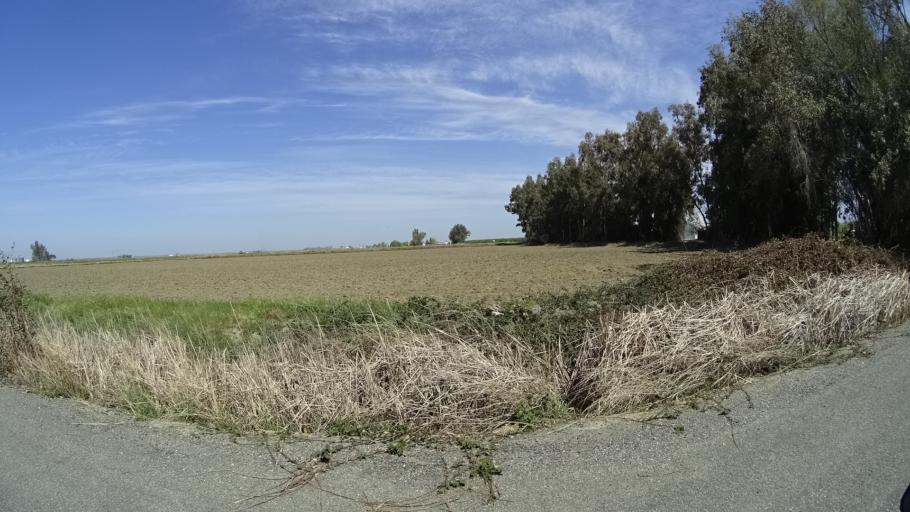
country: US
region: California
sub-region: Glenn County
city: Willows
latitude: 39.5948
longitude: -122.0610
